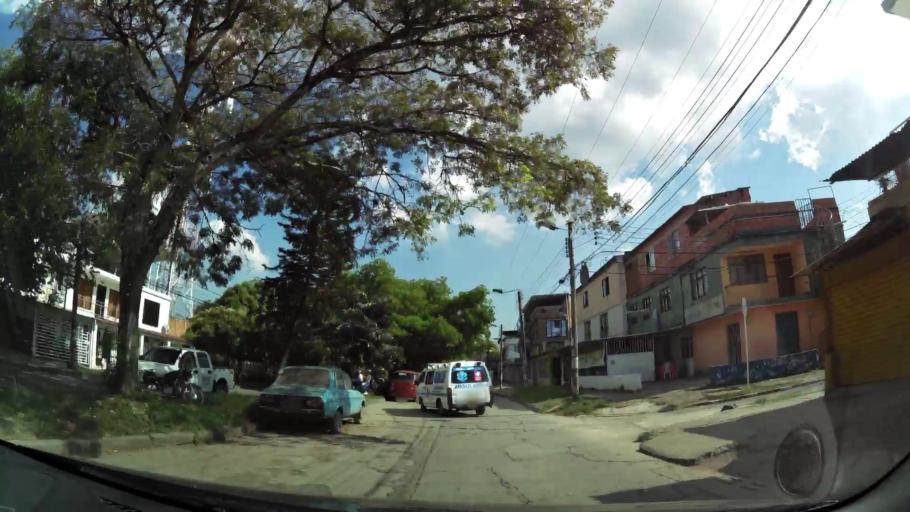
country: CO
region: Valle del Cauca
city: Cali
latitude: 3.4159
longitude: -76.5150
